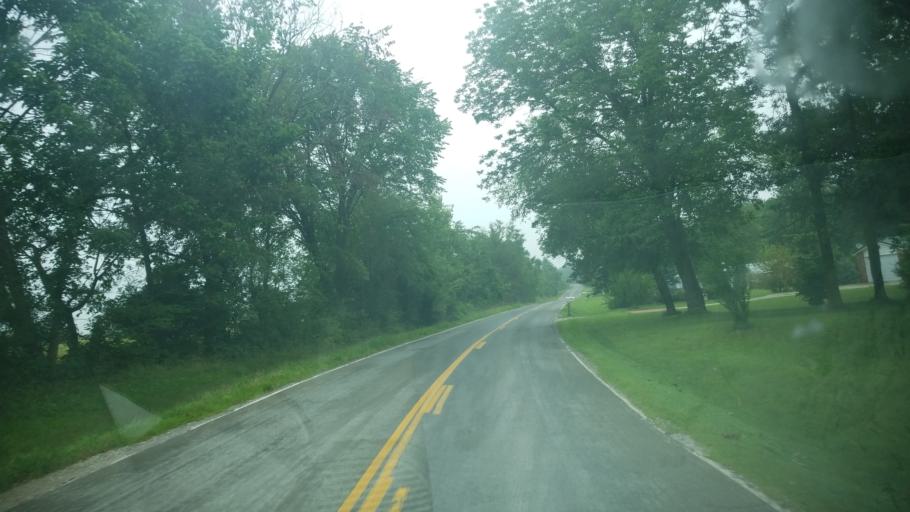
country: US
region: Missouri
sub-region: Audrain County
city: Vandalia
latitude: 39.3021
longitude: -91.3500
